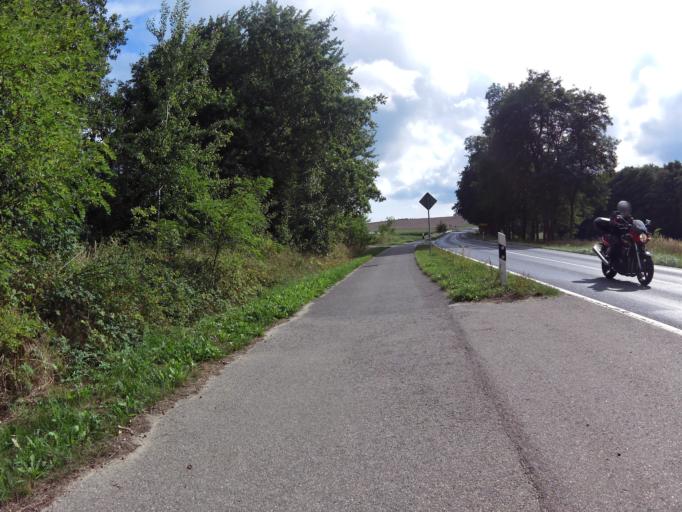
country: DE
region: Mecklenburg-Vorpommern
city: Seebad Bansin
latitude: 53.9602
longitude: 14.0622
